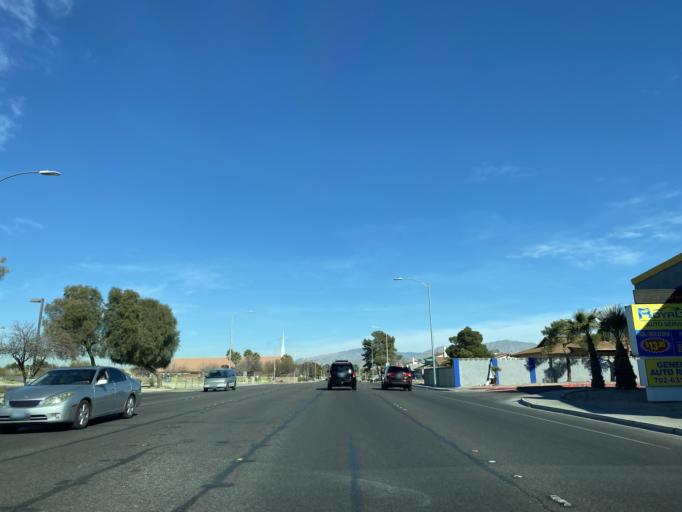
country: US
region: Nevada
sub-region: Clark County
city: Las Vegas
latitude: 36.2038
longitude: -115.2238
